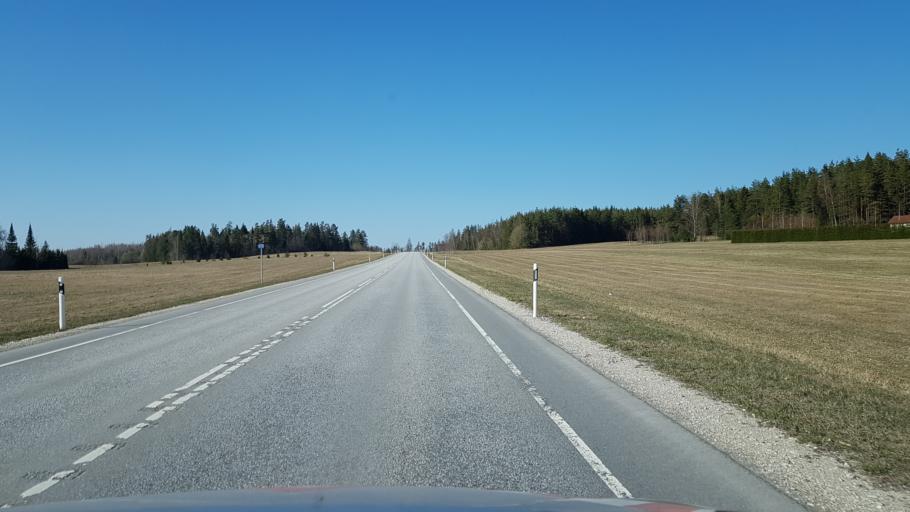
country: EE
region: Tartu
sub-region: Tartu linn
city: Tartu
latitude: 58.5065
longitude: 26.7728
